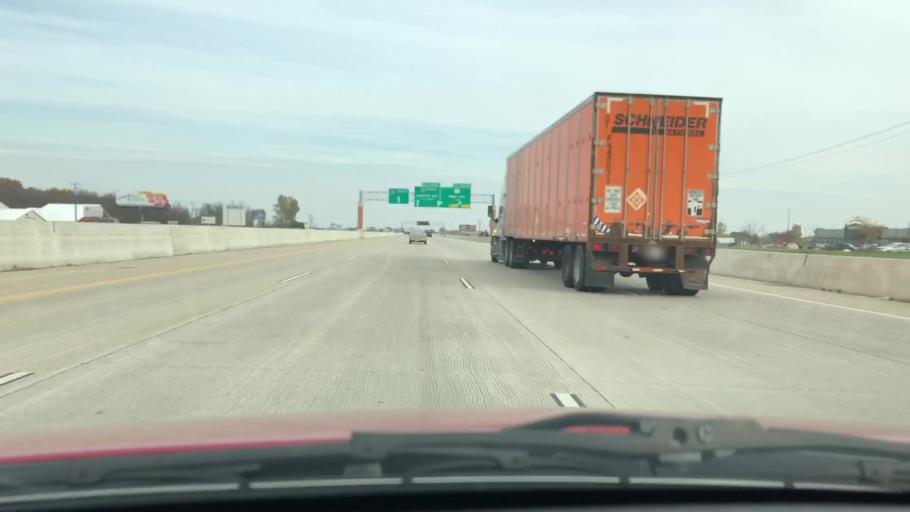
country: US
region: Wisconsin
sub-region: Brown County
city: De Pere
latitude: 44.4342
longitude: -88.1063
